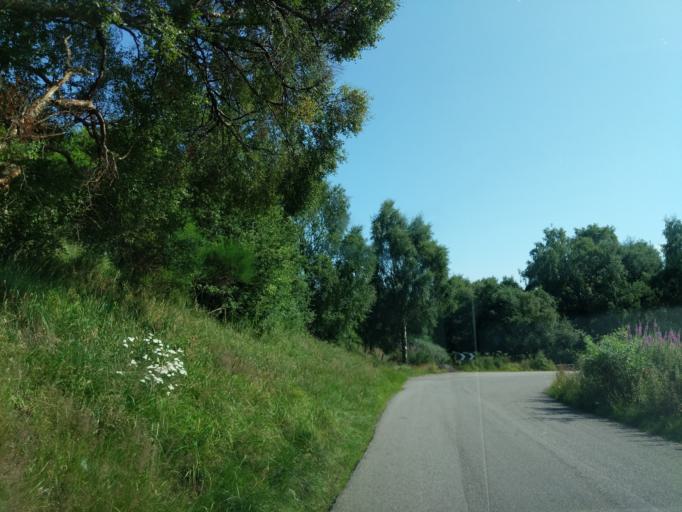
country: GB
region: Scotland
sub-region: Moray
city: Rothes
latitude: 57.4883
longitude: -3.2216
